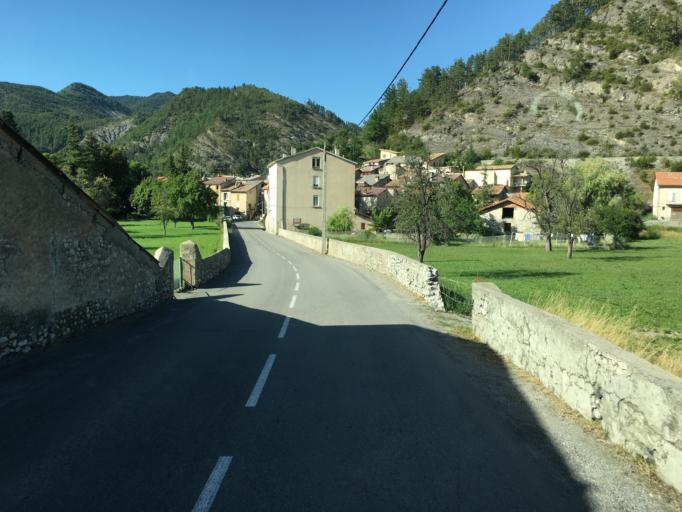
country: FR
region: Provence-Alpes-Cote d'Azur
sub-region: Departement des Alpes-de-Haute-Provence
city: Le Brusquet
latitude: 44.1725
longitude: 6.3505
